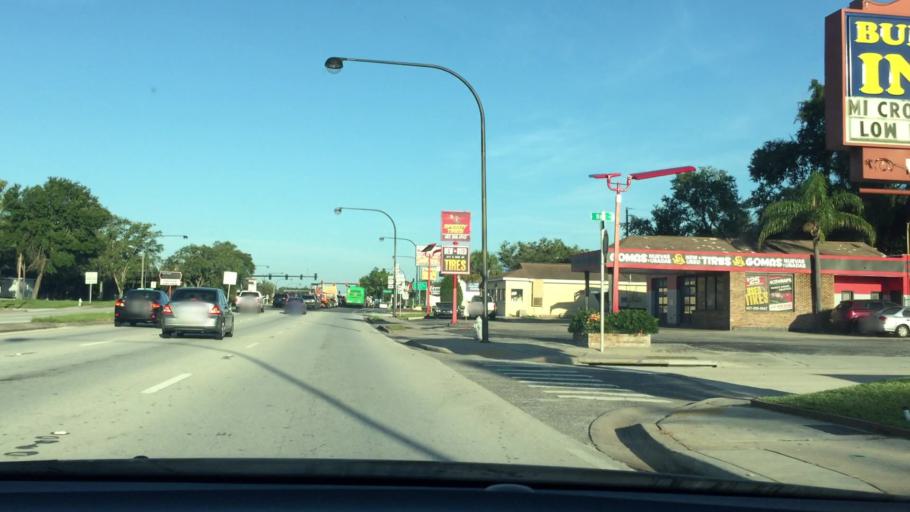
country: US
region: Florida
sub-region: Osceola County
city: Kissimmee
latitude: 28.3045
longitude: -81.4013
